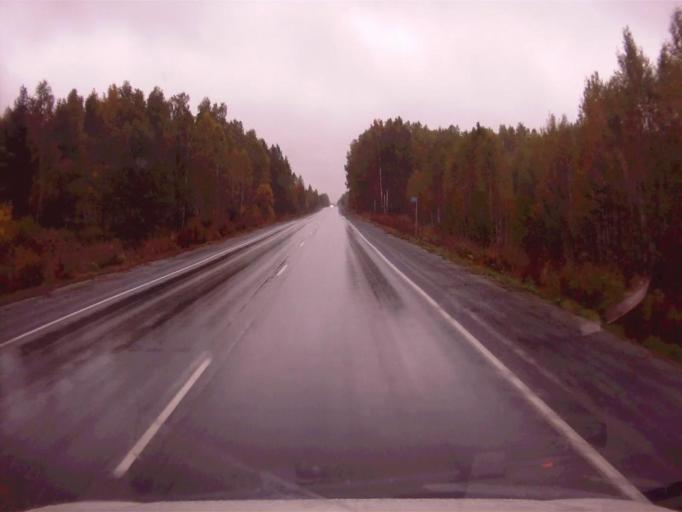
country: RU
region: Chelyabinsk
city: Tayginka
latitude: 55.5349
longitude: 60.6467
